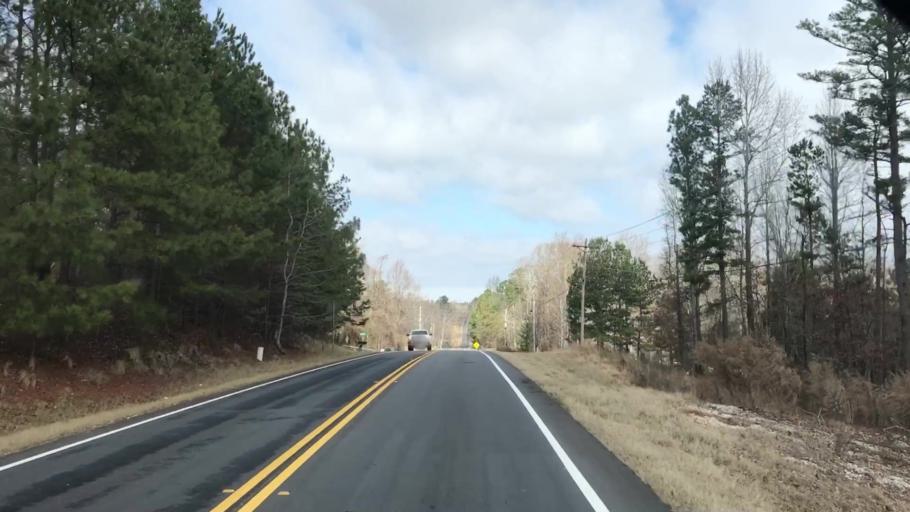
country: US
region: Georgia
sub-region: Jackson County
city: Braselton
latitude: 34.1443
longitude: -83.8380
